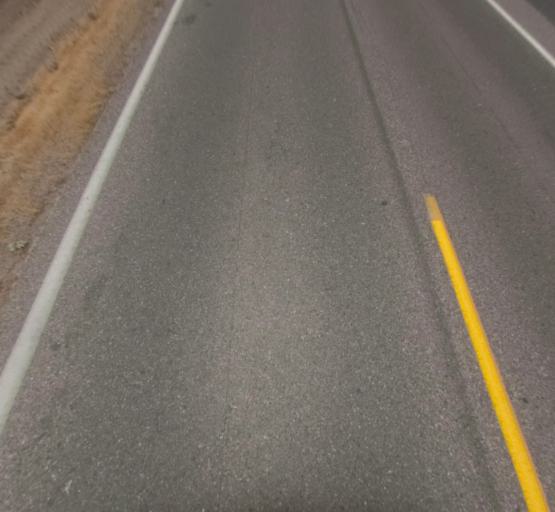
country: US
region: California
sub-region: Madera County
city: Madera
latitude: 36.9237
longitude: -120.1480
